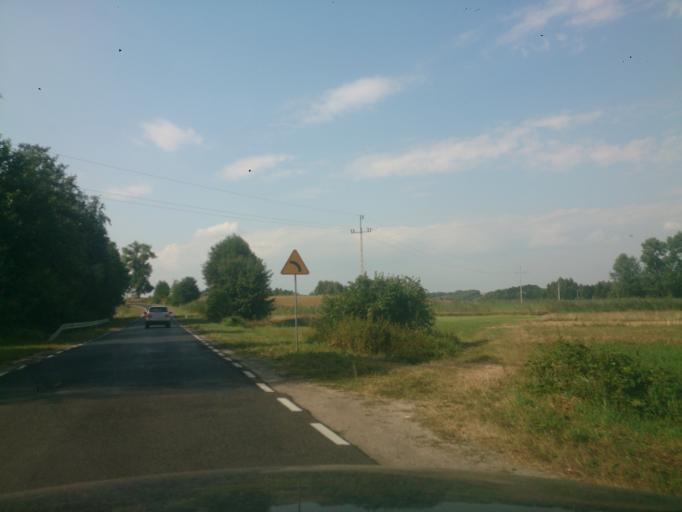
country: PL
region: Swietokrzyskie
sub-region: Powiat sandomierski
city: Klimontow
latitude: 50.6886
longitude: 21.3812
